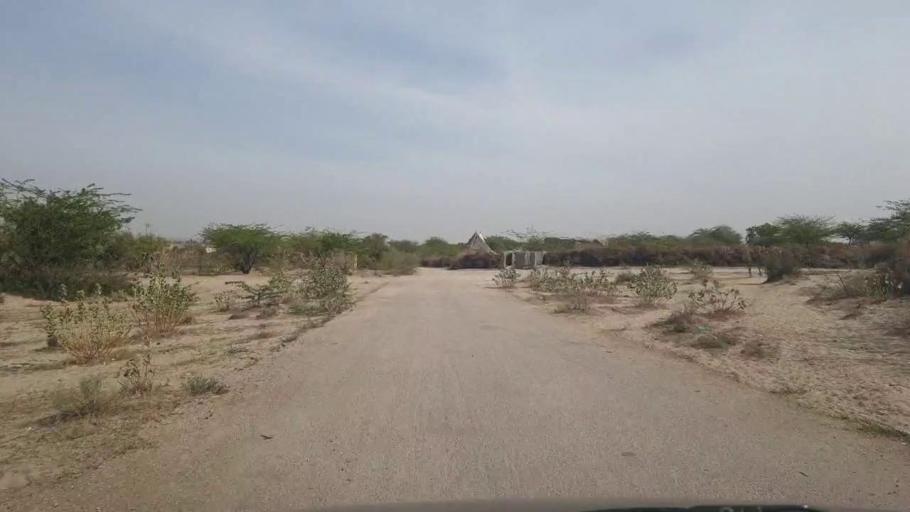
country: PK
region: Sindh
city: Umarkot
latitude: 25.2985
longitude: 69.7412
